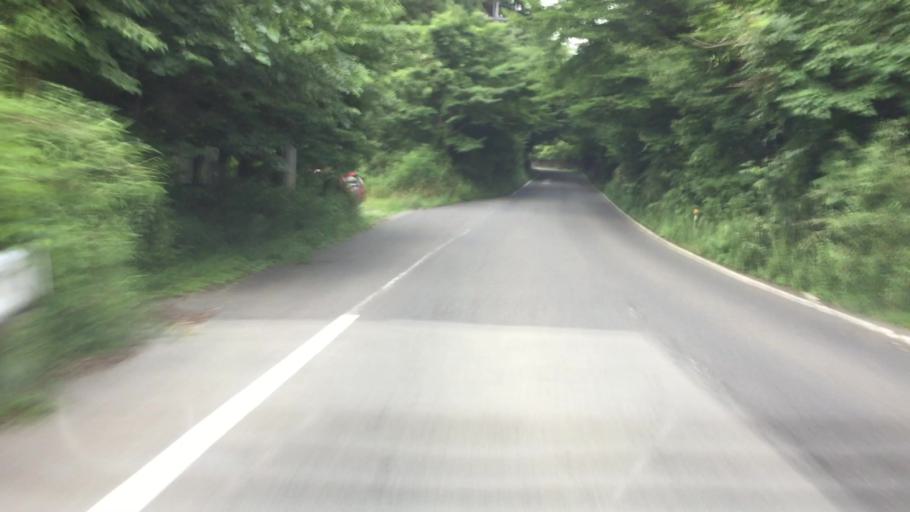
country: JP
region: Tochigi
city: Kuroiso
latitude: 37.0852
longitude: 140.0572
